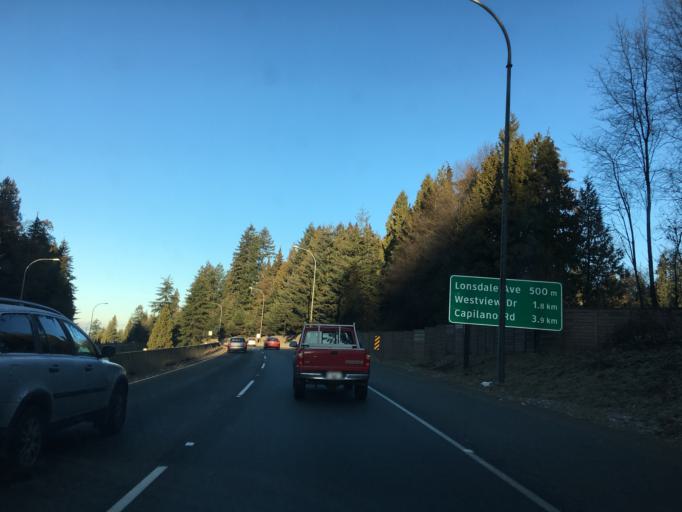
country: CA
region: British Columbia
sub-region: Fraser Valley Regional District
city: North Vancouver
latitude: 49.3317
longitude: -123.0575
